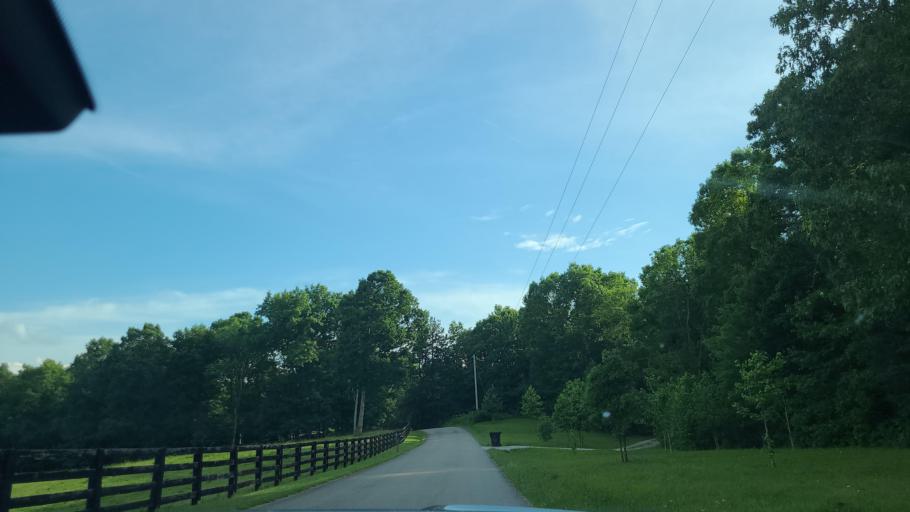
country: US
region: Kentucky
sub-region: Whitley County
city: Corbin
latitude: 36.8855
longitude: -84.2359
